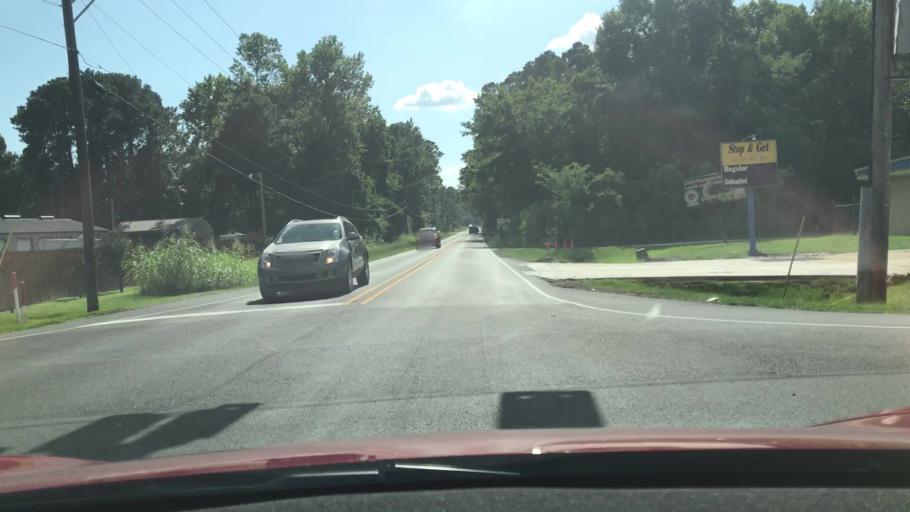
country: US
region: Louisiana
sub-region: De Soto Parish
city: Stonewall
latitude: 32.3910
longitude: -93.7635
